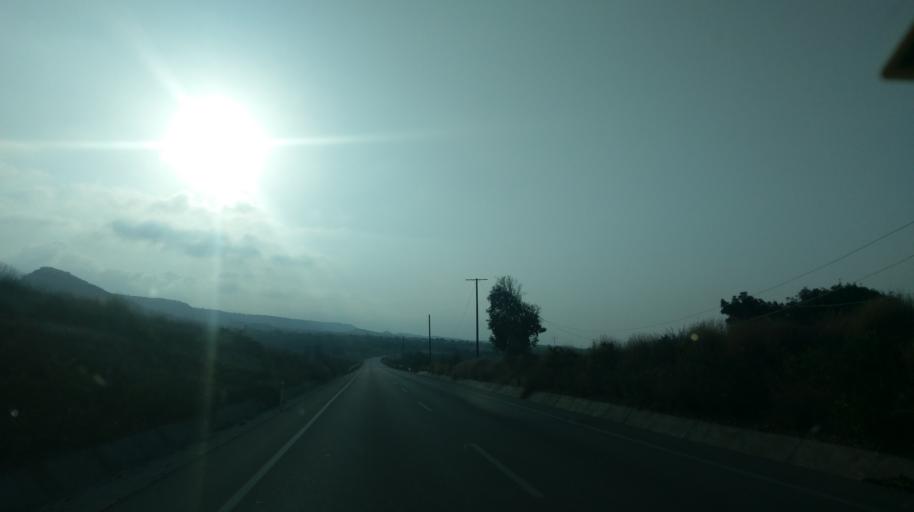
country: CY
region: Ammochostos
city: Trikomo
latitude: 35.4324
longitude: 33.9368
